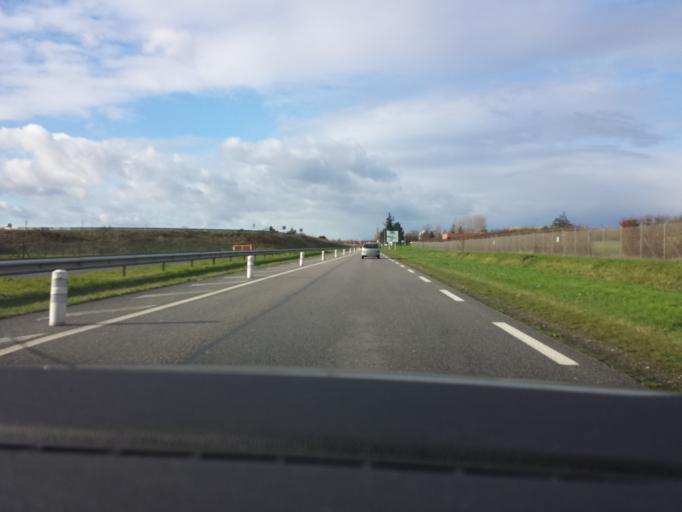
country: FR
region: Haute-Normandie
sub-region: Departement de l'Eure
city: Gravigny
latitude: 49.0151
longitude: 1.1998
